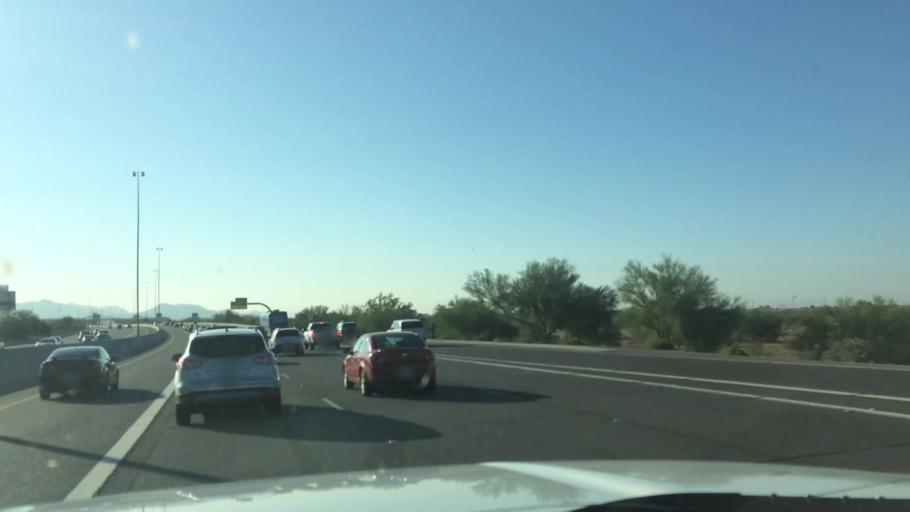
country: US
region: Arizona
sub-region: Maricopa County
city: Paradise Valley
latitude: 33.6681
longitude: -111.9536
